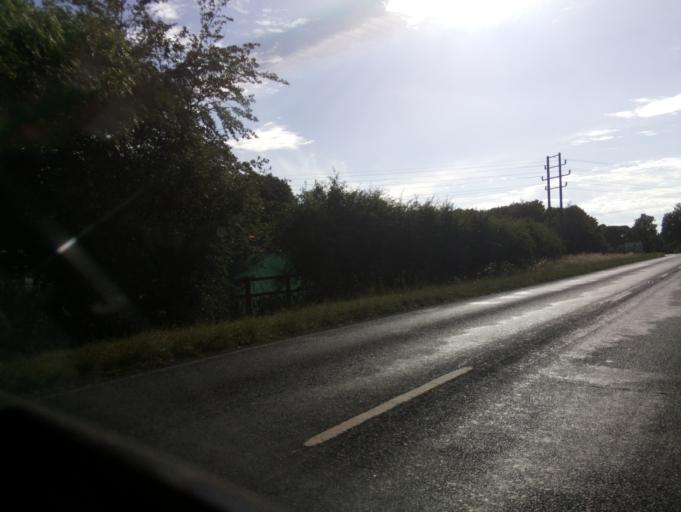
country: GB
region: England
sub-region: Hampshire
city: Romsey
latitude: 50.9846
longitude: -1.4592
